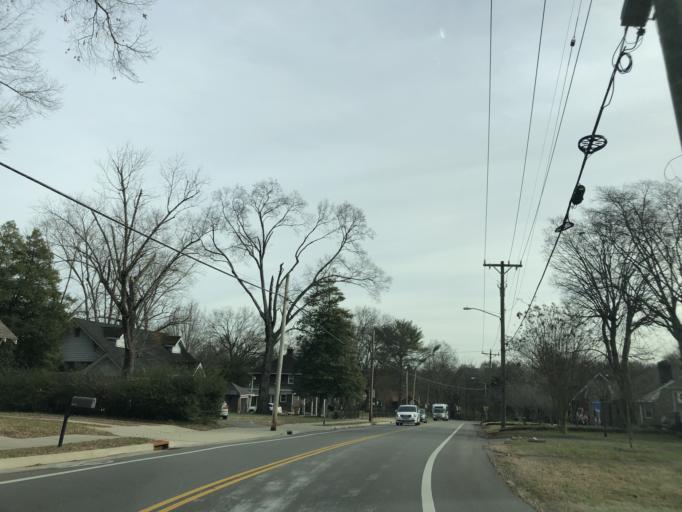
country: US
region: Tennessee
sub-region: Davidson County
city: Nashville
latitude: 36.2098
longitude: -86.7249
